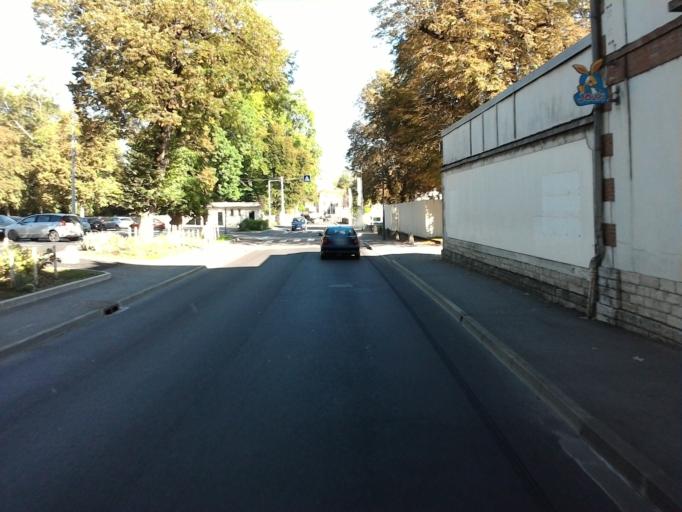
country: FR
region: Bourgogne
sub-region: Departement de la Cote-d'Or
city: Chatillon-sur-Seine
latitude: 47.8628
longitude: 4.5748
